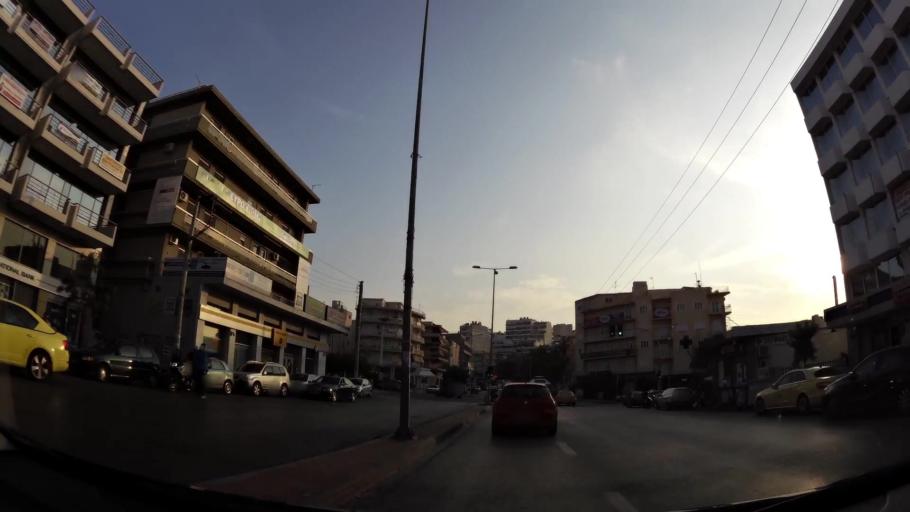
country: GR
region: Attica
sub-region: Nomarchia Athinas
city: Galatsi
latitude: 38.0134
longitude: 23.7531
